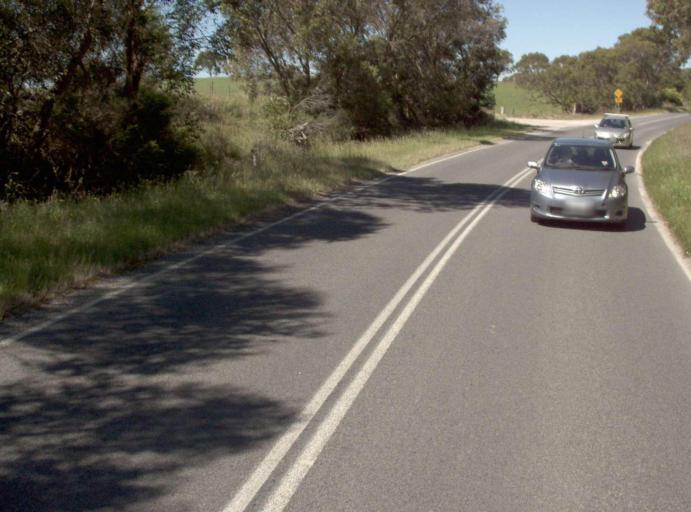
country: AU
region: Victoria
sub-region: Bass Coast
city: North Wonthaggi
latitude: -38.7453
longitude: 146.1383
